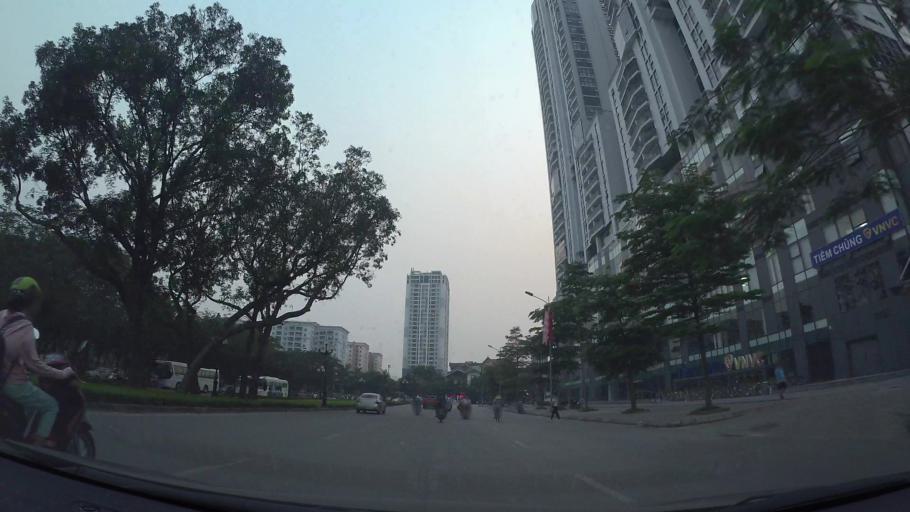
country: VN
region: Ha Noi
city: Ha Dong
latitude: 20.9764
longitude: 105.7903
